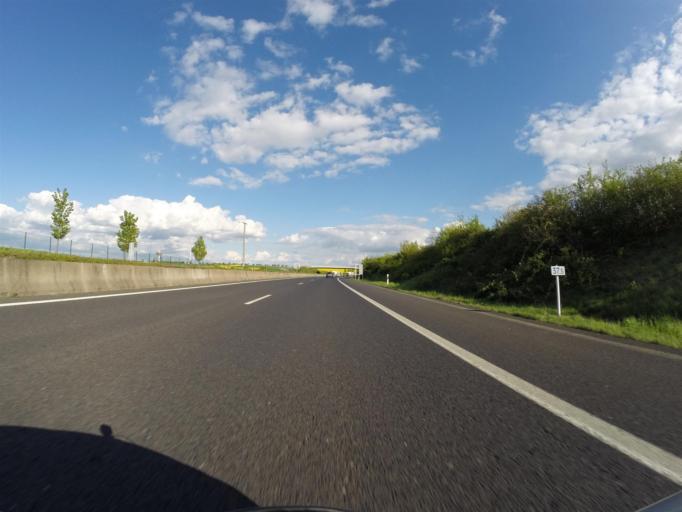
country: LU
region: Grevenmacher
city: Schengen
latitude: 49.4921
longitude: 6.3265
